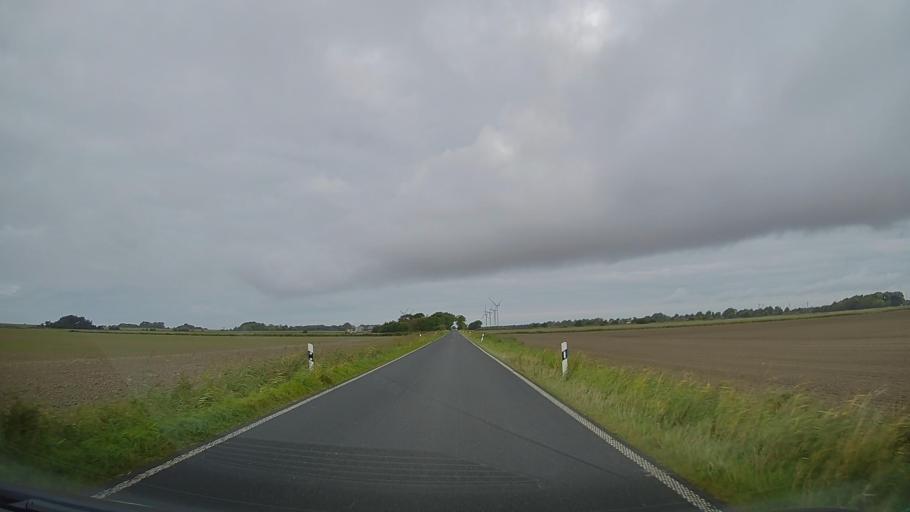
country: DE
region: Schleswig-Holstein
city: Galmsbull
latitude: 54.7576
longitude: 8.7251
